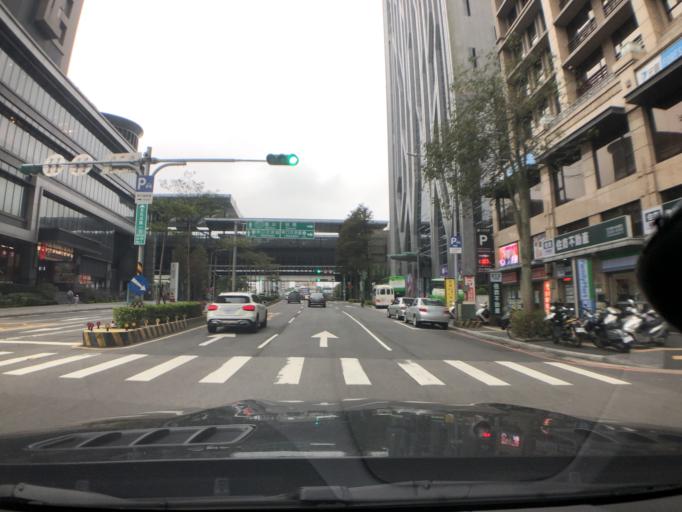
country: TW
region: Taiwan
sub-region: Taoyuan
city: Taoyuan
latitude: 25.0668
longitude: 121.3611
